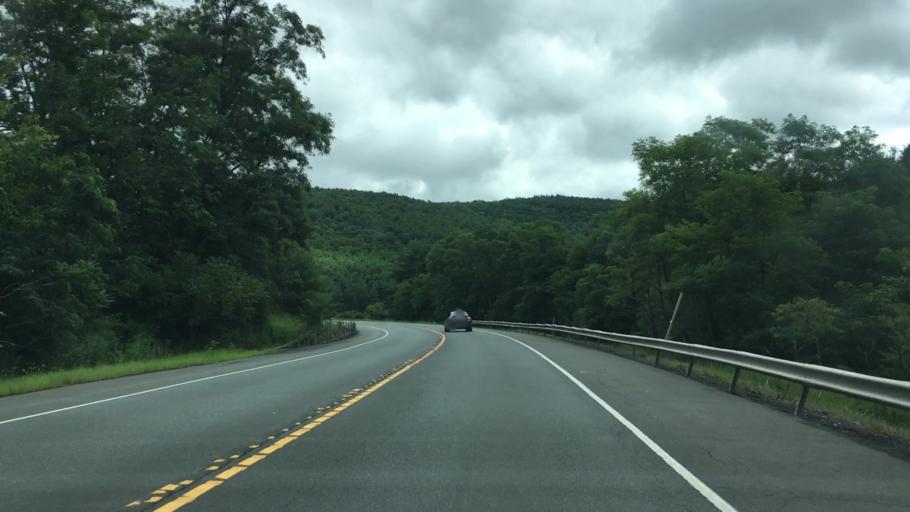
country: US
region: New York
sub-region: Rensselaer County
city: Hoosick Falls
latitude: 42.8423
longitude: -73.3804
